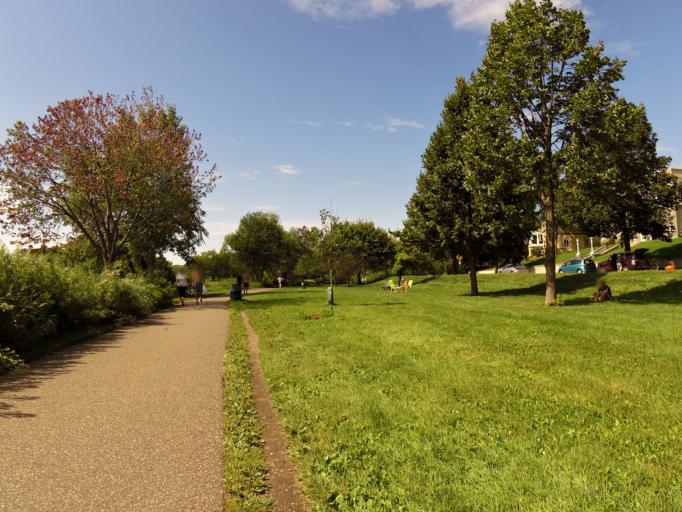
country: US
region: Minnesota
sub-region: Hennepin County
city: Minneapolis
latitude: 44.9558
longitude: -93.3024
